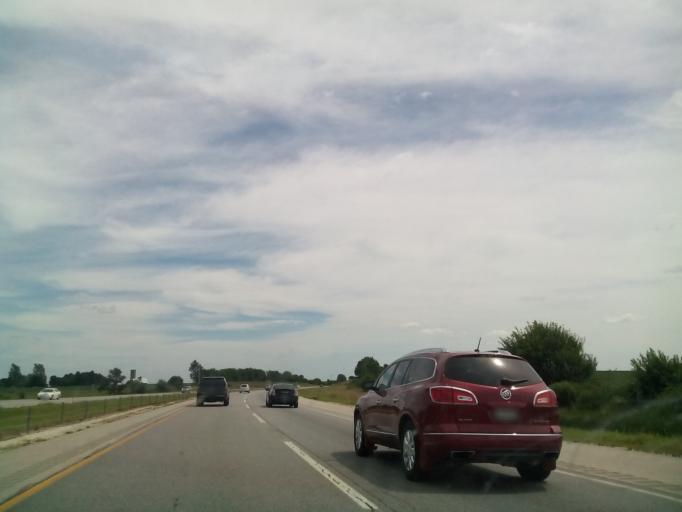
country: US
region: Illinois
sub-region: DeKalb County
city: Cortland
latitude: 41.9003
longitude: -88.6490
